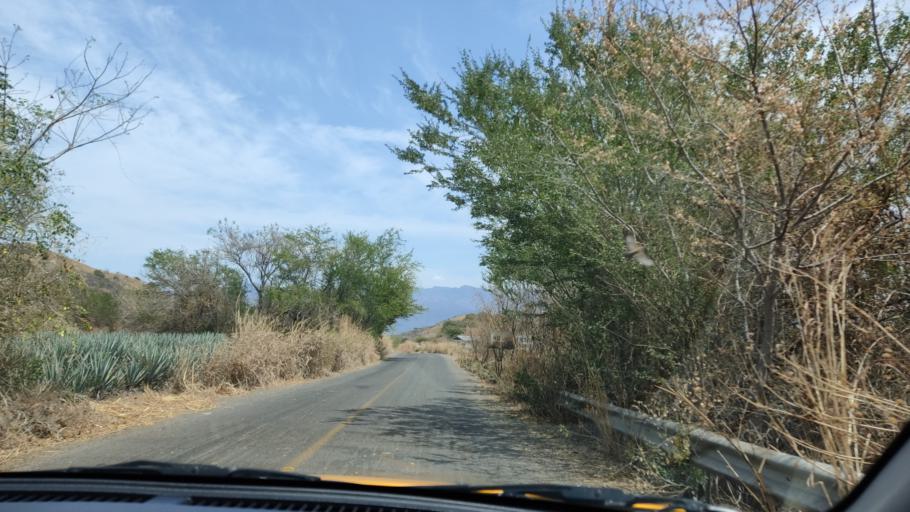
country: MX
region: Nayarit
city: Santa Maria del Oro
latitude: 21.5005
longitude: -104.6178
